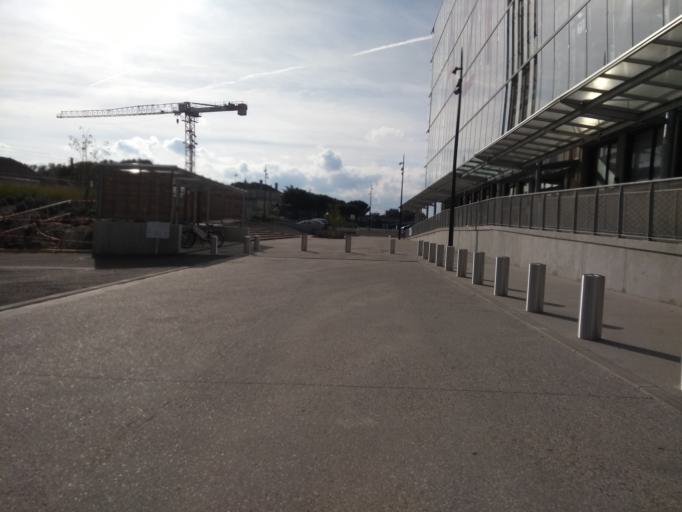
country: FR
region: Aquitaine
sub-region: Departement de la Gironde
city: Talence
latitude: 44.8066
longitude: -0.5976
